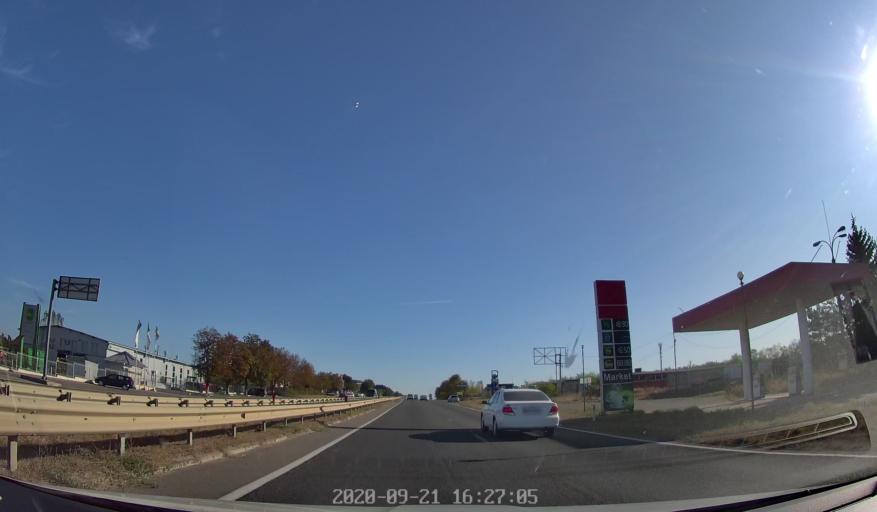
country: MD
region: Chisinau
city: Stauceni
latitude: 47.1086
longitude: 28.8600
